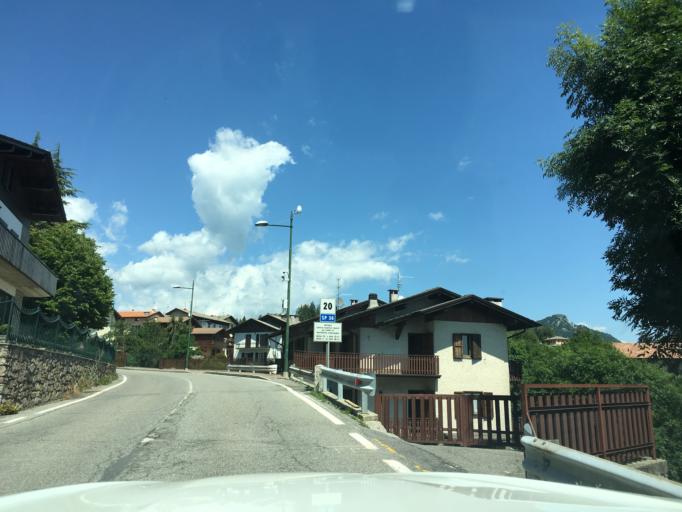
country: IT
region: Lombardy
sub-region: Provincia di Bergamo
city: Selvino
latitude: 45.7773
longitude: 9.7431
